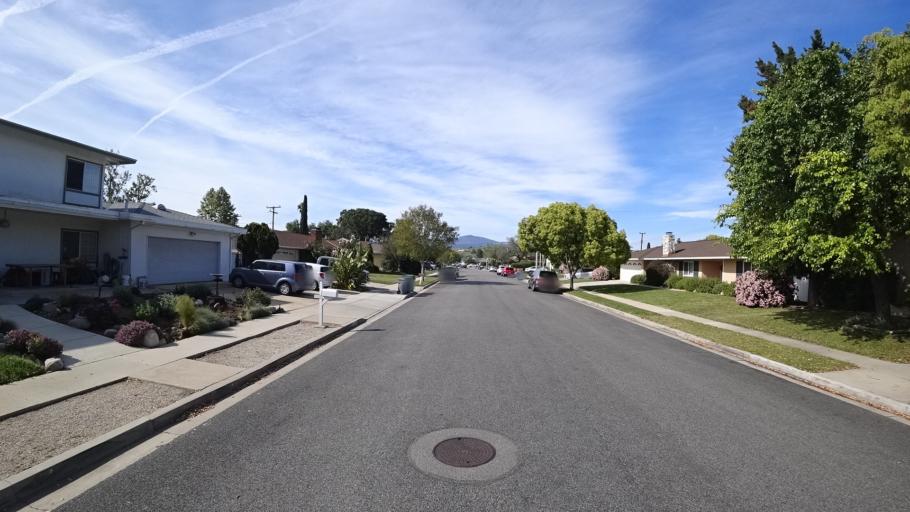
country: US
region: California
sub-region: Ventura County
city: Thousand Oaks
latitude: 34.1980
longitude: -118.8735
